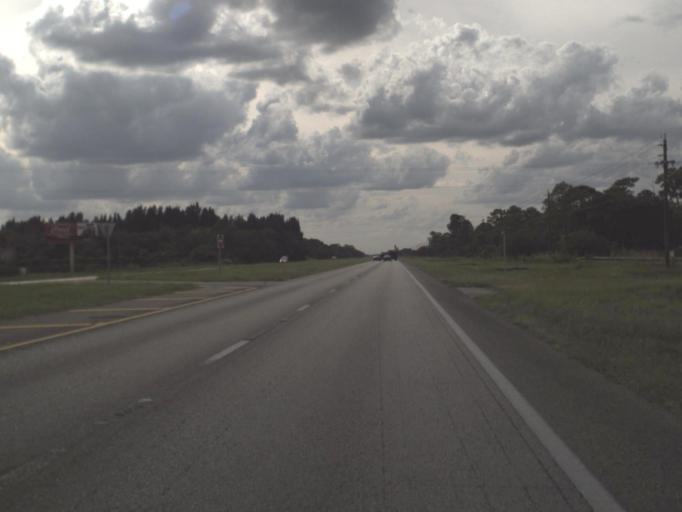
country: US
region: Florida
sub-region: Lee County
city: Alva
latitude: 26.7098
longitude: -81.5411
